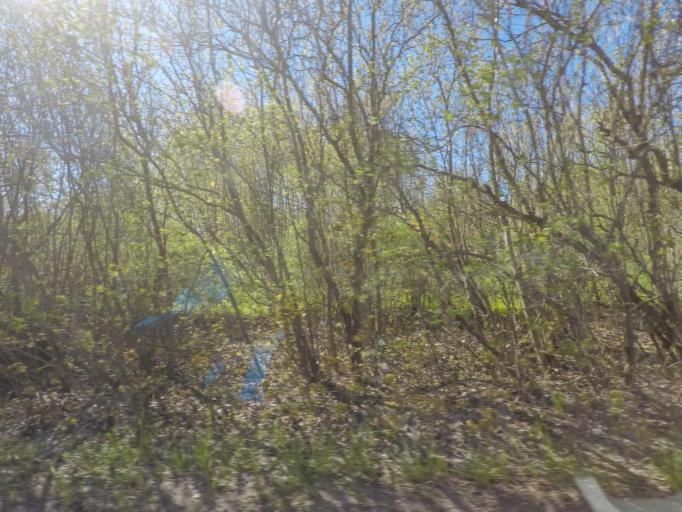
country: FI
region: Uusimaa
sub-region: Helsinki
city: Sammatti
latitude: 60.3223
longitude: 23.8180
